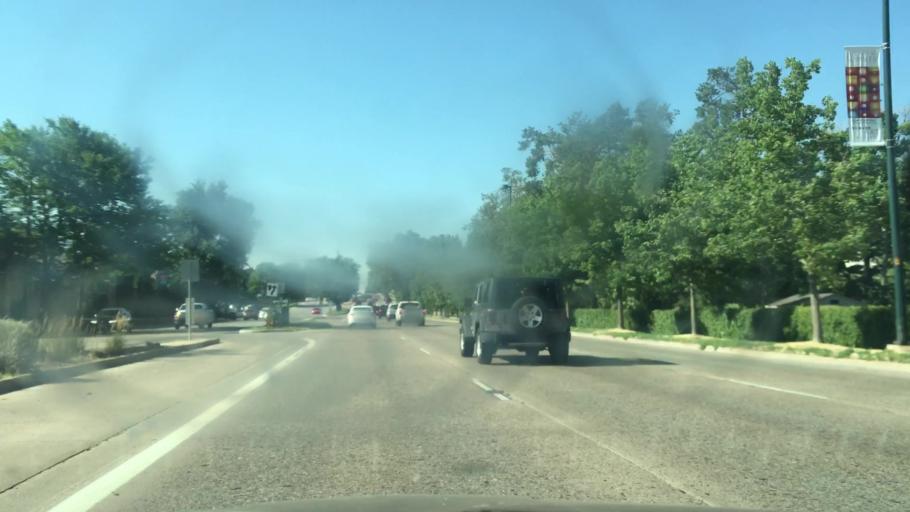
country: US
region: Colorado
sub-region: Arapahoe County
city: Glendale
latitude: 39.7143
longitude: -104.9593
